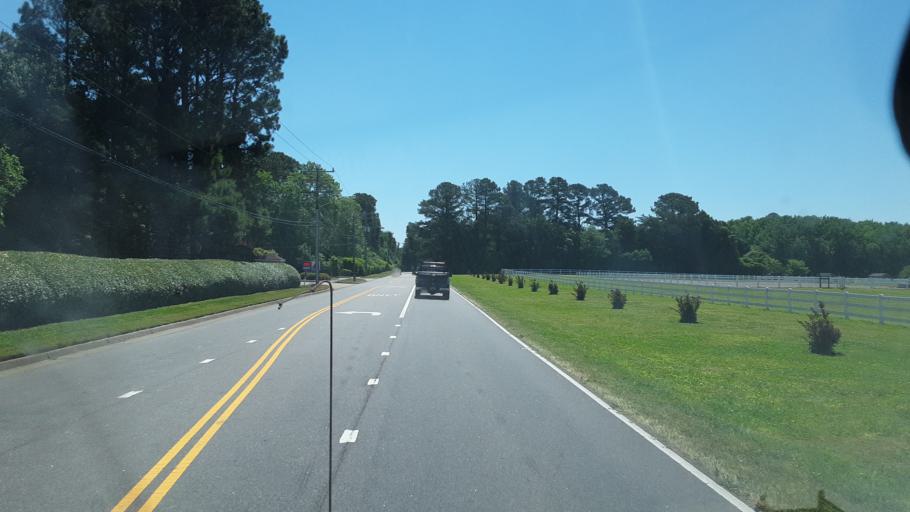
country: US
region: Virginia
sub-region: City of Virginia Beach
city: Virginia Beach
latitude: 36.7461
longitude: -75.9957
